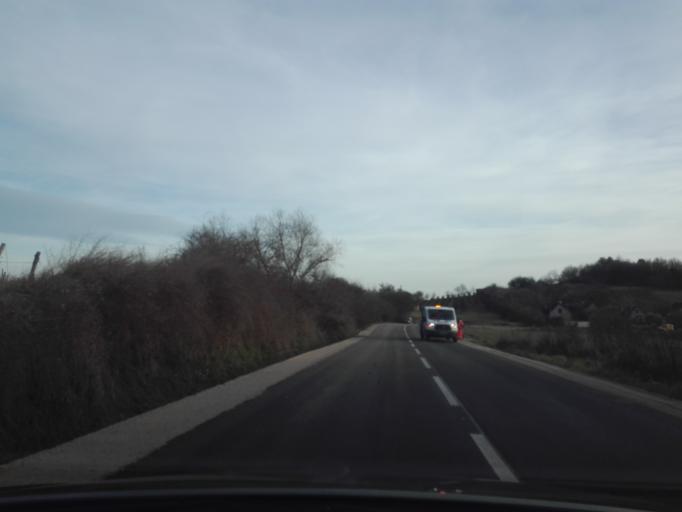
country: HU
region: Veszprem
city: Balatonfured
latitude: 46.9800
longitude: 17.8230
